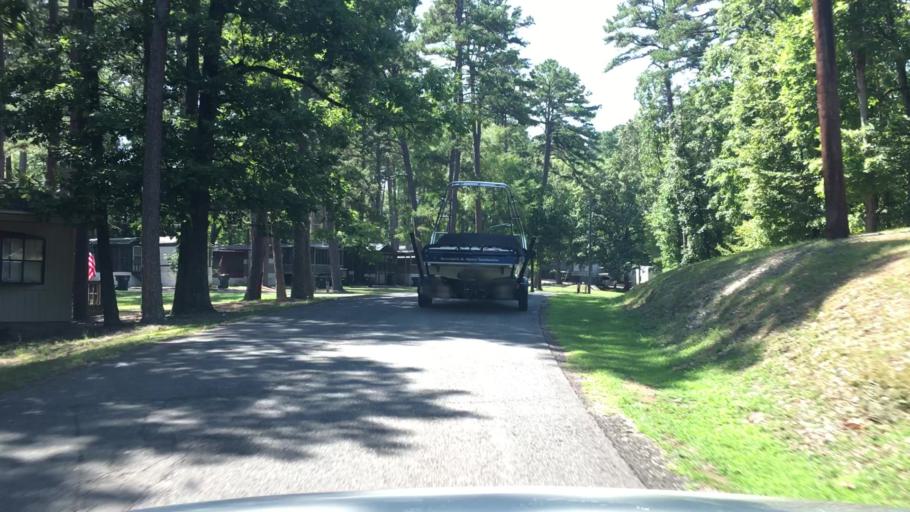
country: US
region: Arkansas
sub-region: Garland County
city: Piney
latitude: 34.5438
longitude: -93.3598
